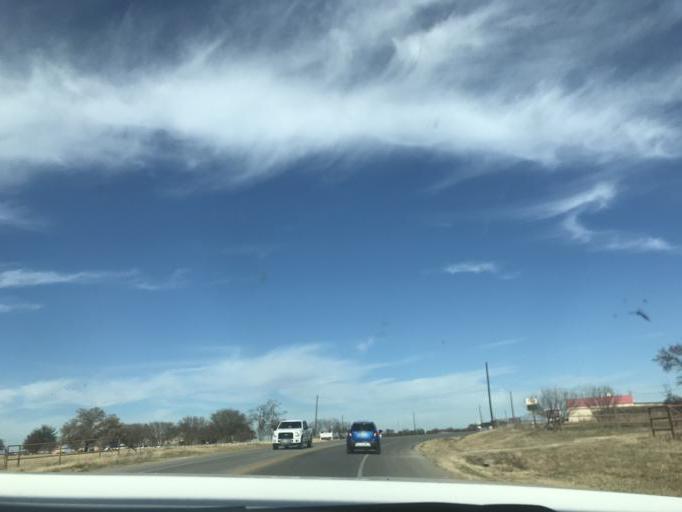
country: US
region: Texas
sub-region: Erath County
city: Stephenville
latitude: 32.2421
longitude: -98.1970
